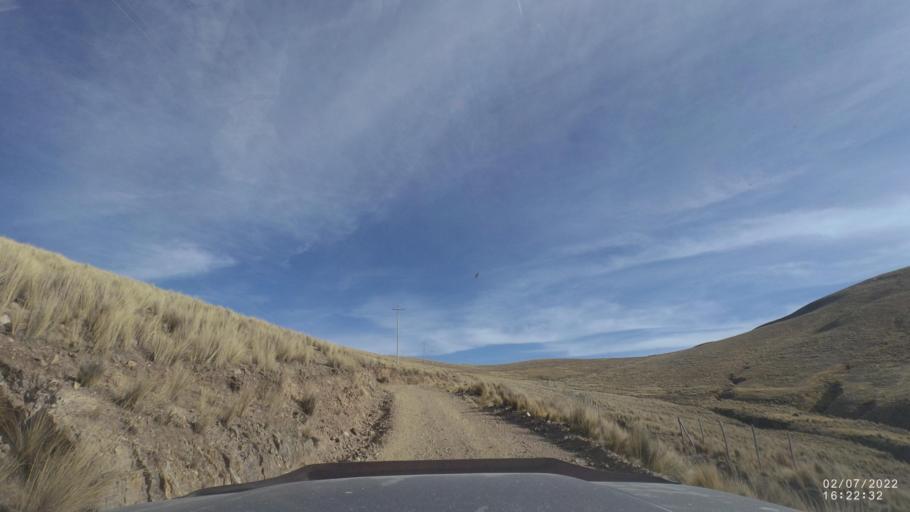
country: BO
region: Cochabamba
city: Irpa Irpa
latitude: -17.9357
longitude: -66.4560
